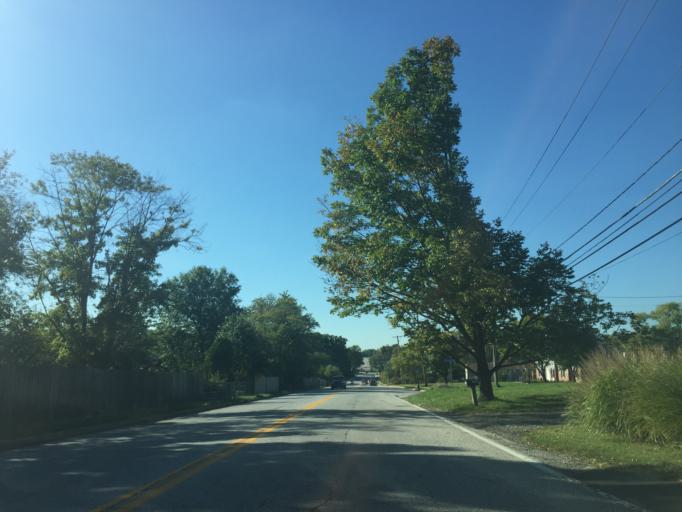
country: US
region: Maryland
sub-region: Baltimore County
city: Rossville
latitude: 39.3560
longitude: -76.4661
